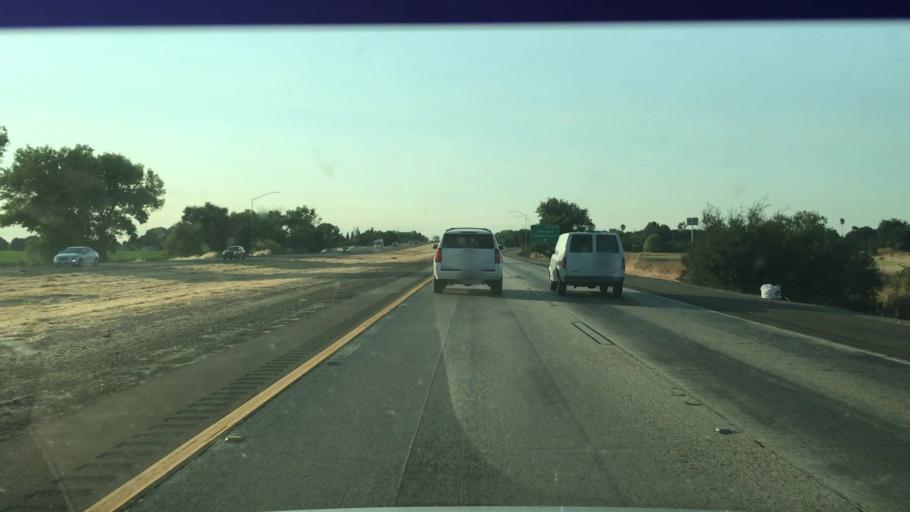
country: US
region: California
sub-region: San Joaquin County
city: Thornton
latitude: 38.2211
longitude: -121.4271
